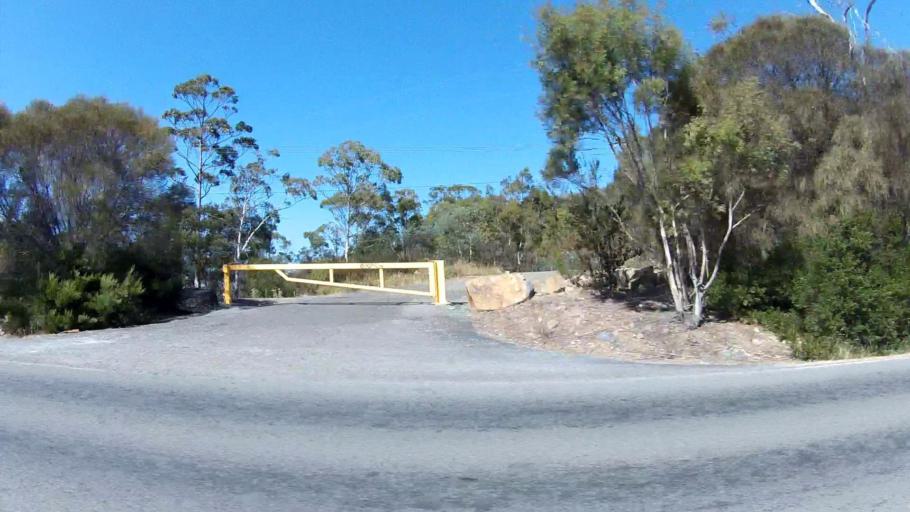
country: AU
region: Tasmania
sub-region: Sorell
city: Sorell
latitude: -42.5597
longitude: 147.8475
